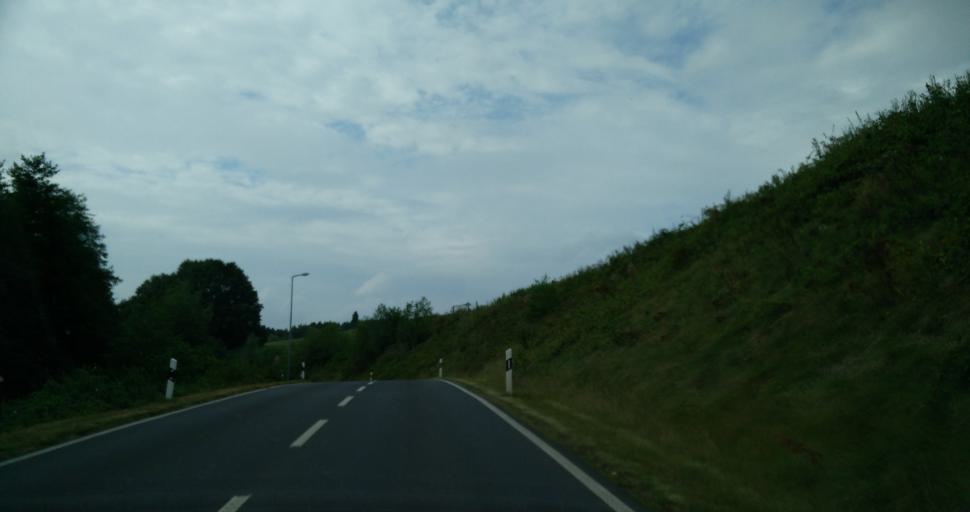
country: DE
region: North Rhine-Westphalia
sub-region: Regierungsbezirk Dusseldorf
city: Ratingen
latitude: 51.2832
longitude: 6.8800
